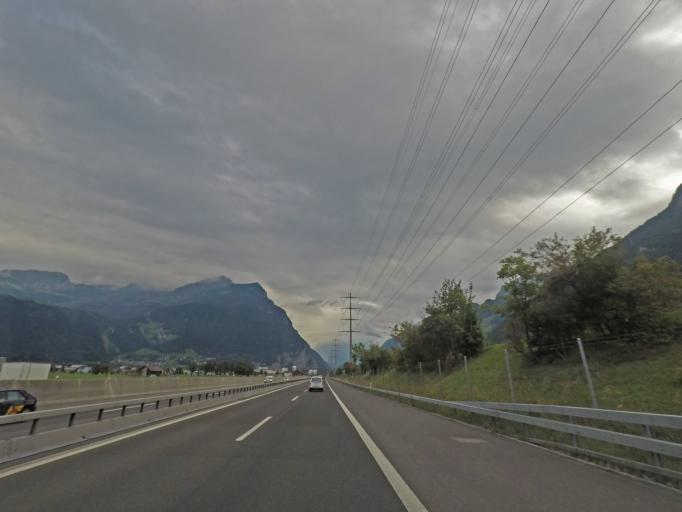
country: CH
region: Uri
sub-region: Uri
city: Seedorf
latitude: 46.8818
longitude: 8.6226
